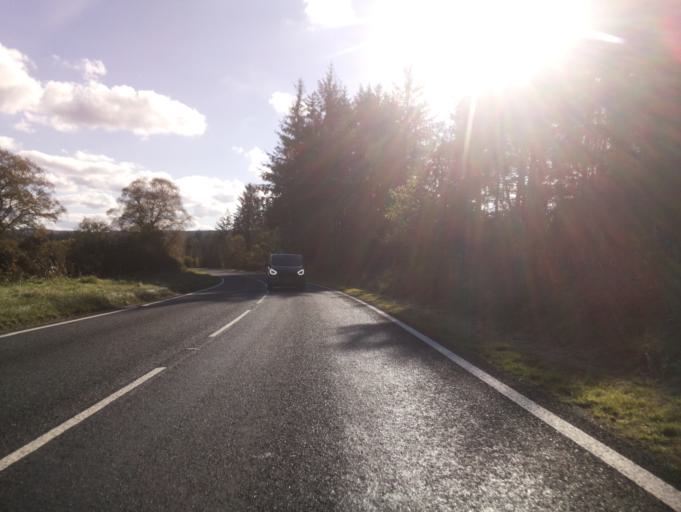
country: GB
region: Wales
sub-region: Merthyr Tydfil County Borough
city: Merthyr Tydfil
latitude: 51.8131
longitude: -3.4446
